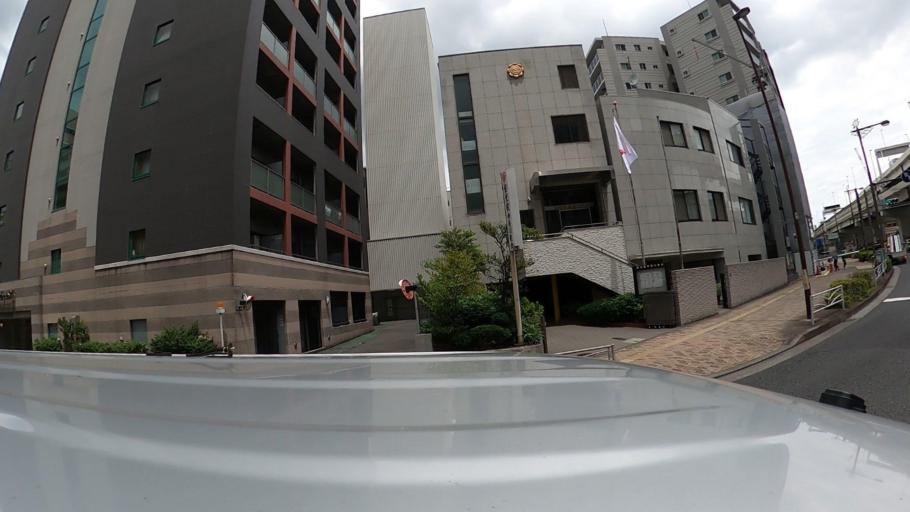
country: JP
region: Kanagawa
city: Yokohama
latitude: 35.4700
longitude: 139.6296
